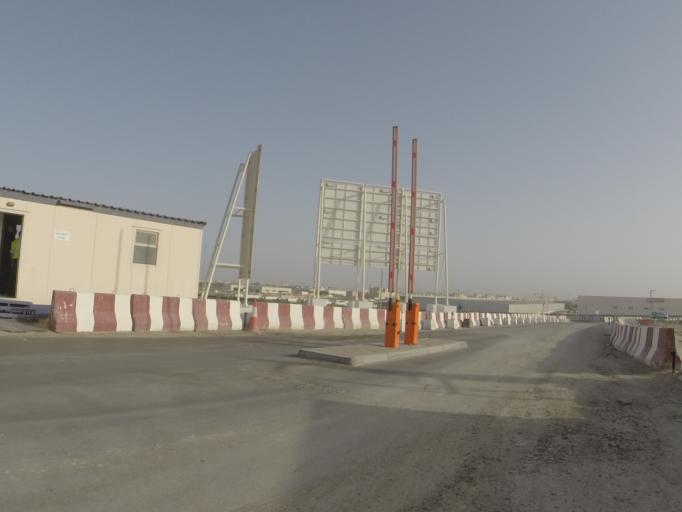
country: AE
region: Dubai
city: Dubai
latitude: 24.9684
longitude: 55.1642
